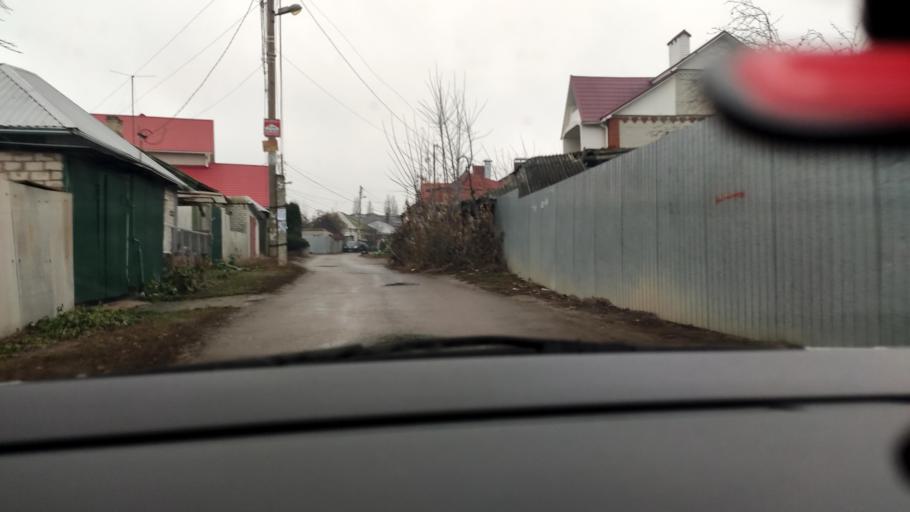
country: RU
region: Voronezj
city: Voronezh
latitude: 51.6481
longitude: 39.2024
